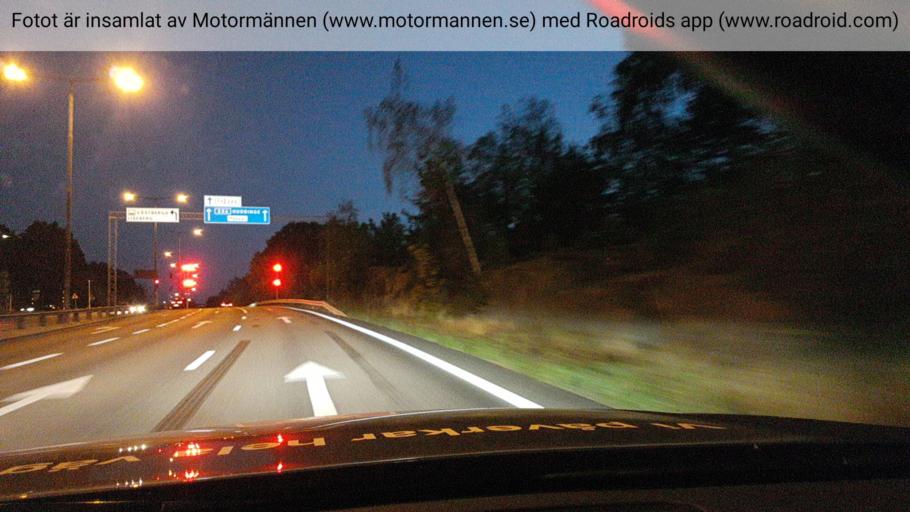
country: SE
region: Stockholm
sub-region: Stockholms Kommun
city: Arsta
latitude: 59.2875
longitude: 18.0209
